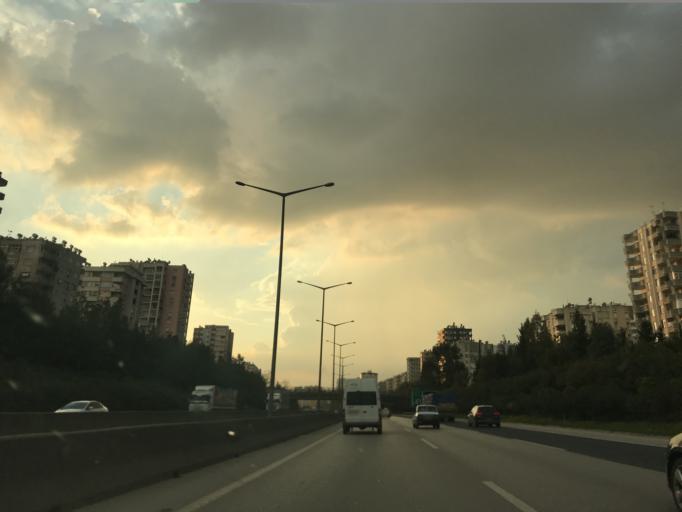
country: TR
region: Adana
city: Adana
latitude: 37.0326
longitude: 35.3032
